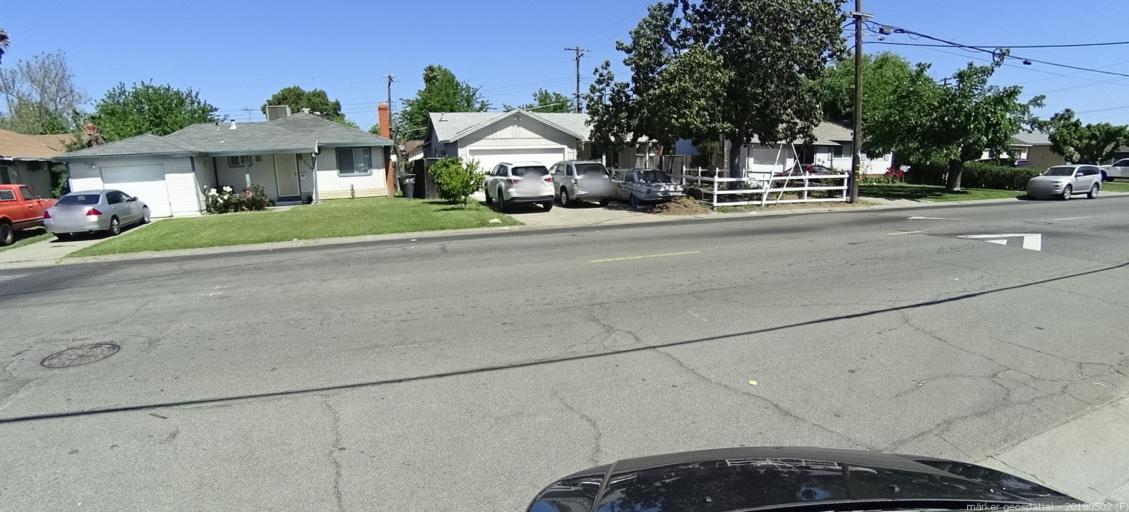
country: US
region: California
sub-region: Sacramento County
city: Arden-Arcade
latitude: 38.6212
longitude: -121.4166
